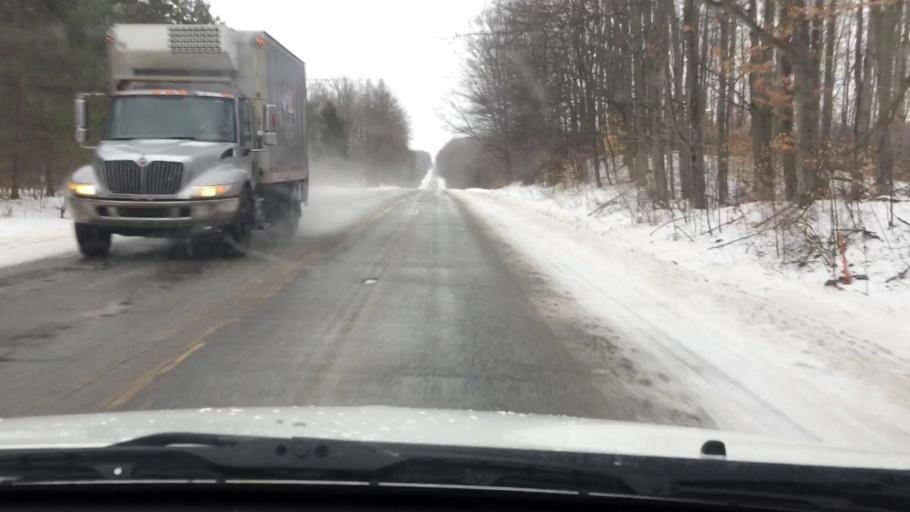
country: US
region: Michigan
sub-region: Wexford County
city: Cadillac
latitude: 44.1954
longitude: -85.4057
